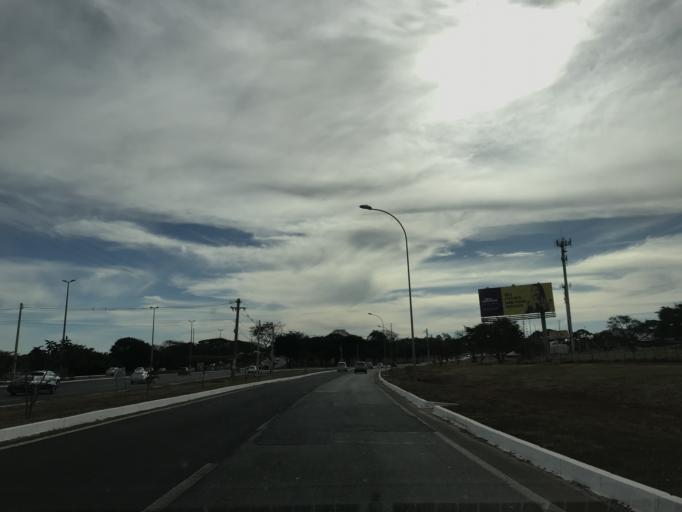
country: BR
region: Federal District
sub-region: Brasilia
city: Brasilia
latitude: -15.8417
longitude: -47.9484
